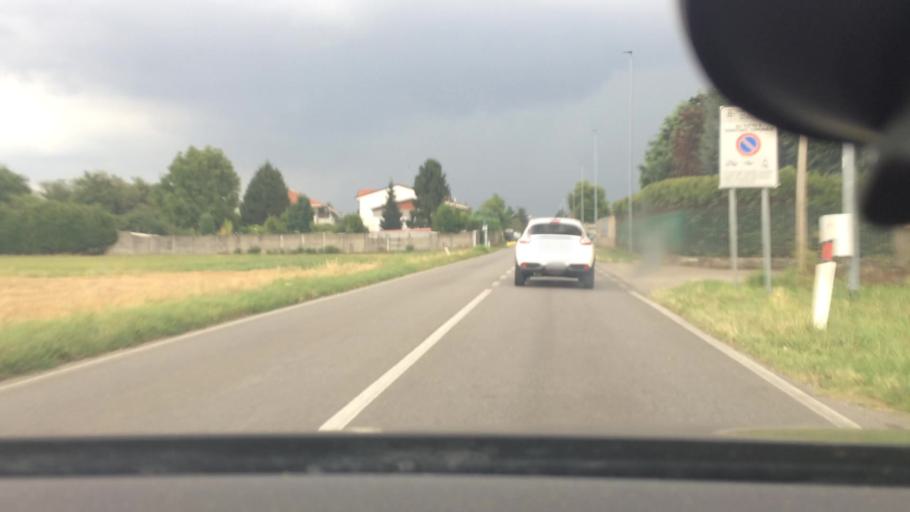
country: IT
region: Lombardy
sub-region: Citta metropolitana di Milano
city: Cantalupo
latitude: 45.5728
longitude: 8.9848
